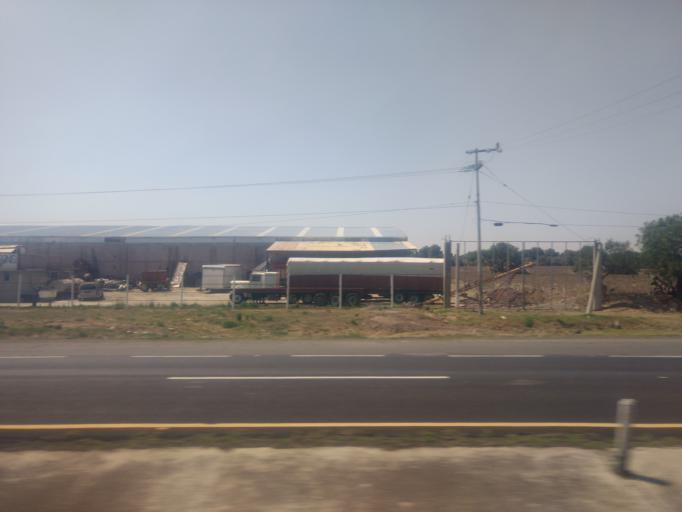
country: MX
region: Morelos
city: Nopaltepec
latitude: 19.7838
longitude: -98.7355
